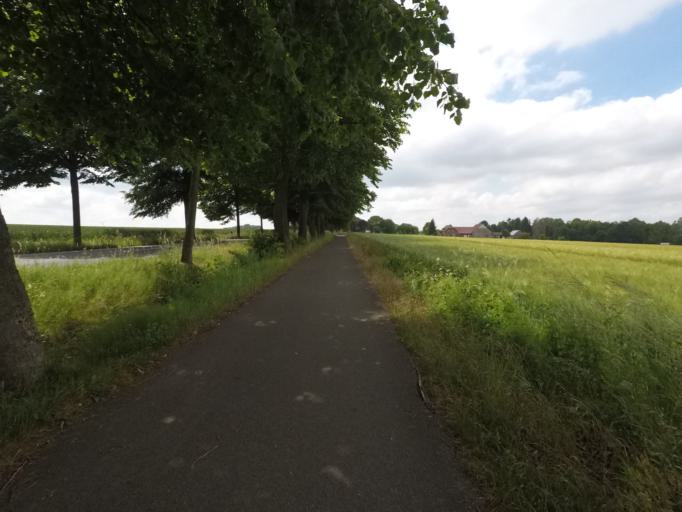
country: DE
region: North Rhine-Westphalia
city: Spenge
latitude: 52.1299
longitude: 8.5087
